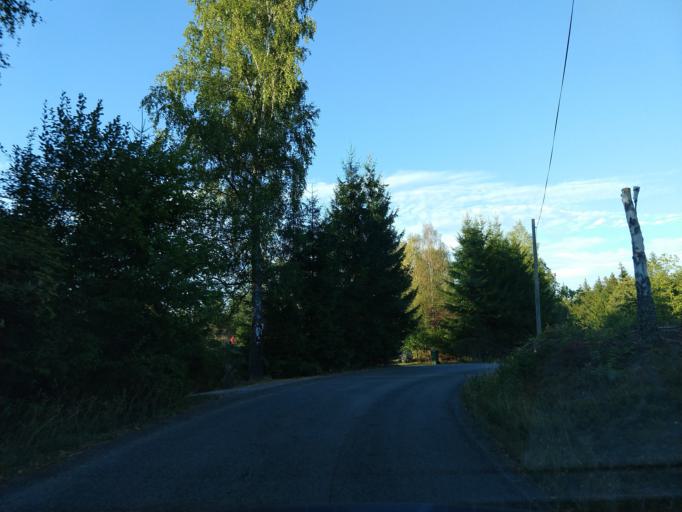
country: SE
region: Blekinge
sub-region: Ronneby Kommun
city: Brakne-Hoby
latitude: 56.2663
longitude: 15.1473
